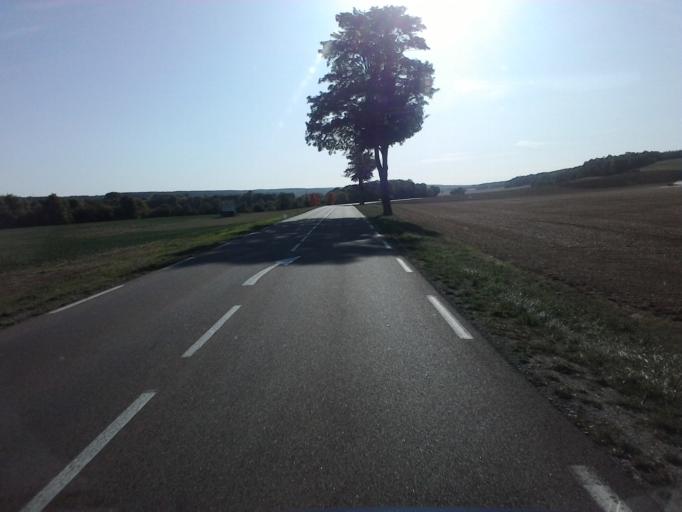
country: FR
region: Champagne-Ardenne
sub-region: Departement de l'Aube
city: Bar-sur-Seine
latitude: 48.1340
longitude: 4.3304
